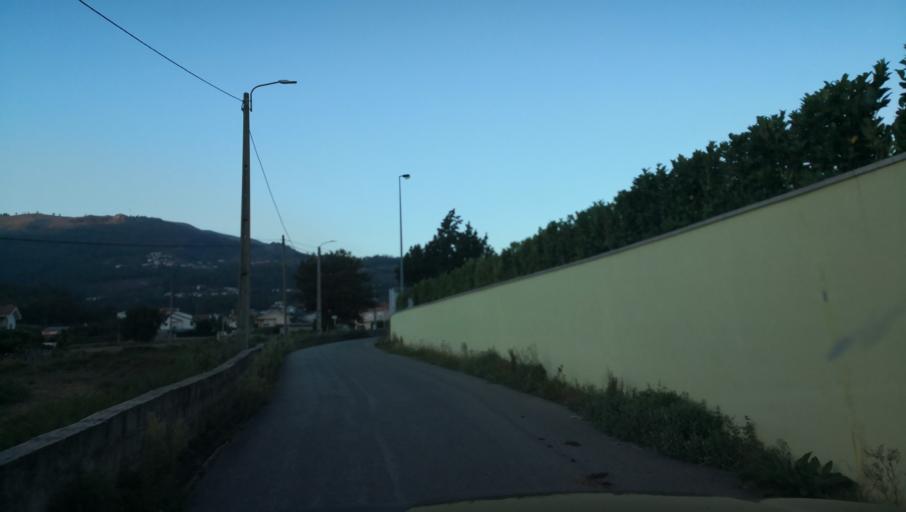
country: PT
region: Vila Real
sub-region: Vila Real
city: Vila Real
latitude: 41.3137
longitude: -7.7712
